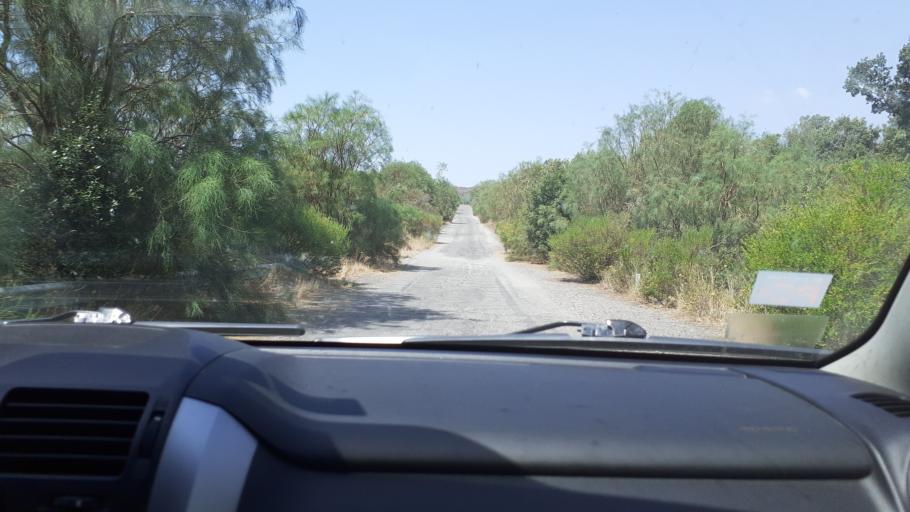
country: IT
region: Sicily
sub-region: Catania
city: Nicolosi
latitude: 37.6464
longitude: 15.0078
